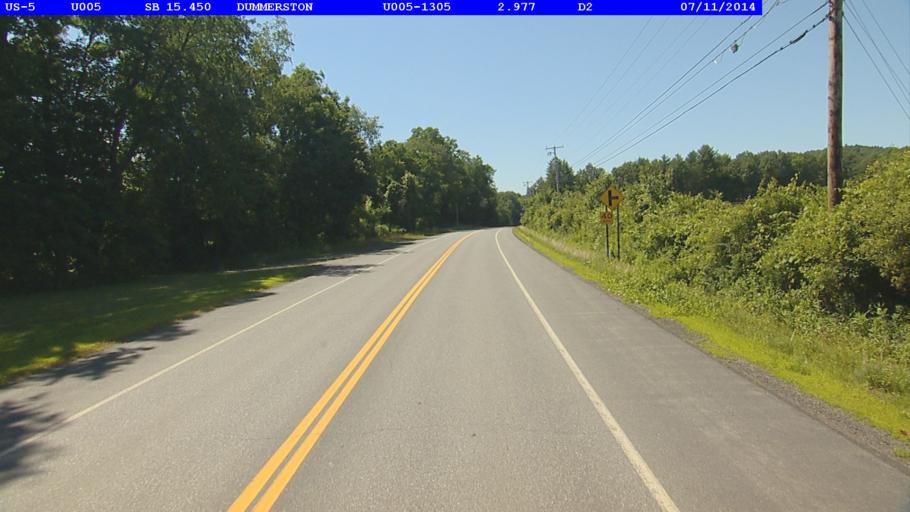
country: US
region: New Hampshire
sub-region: Cheshire County
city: Chesterfield
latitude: 42.9355
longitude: -72.5353
